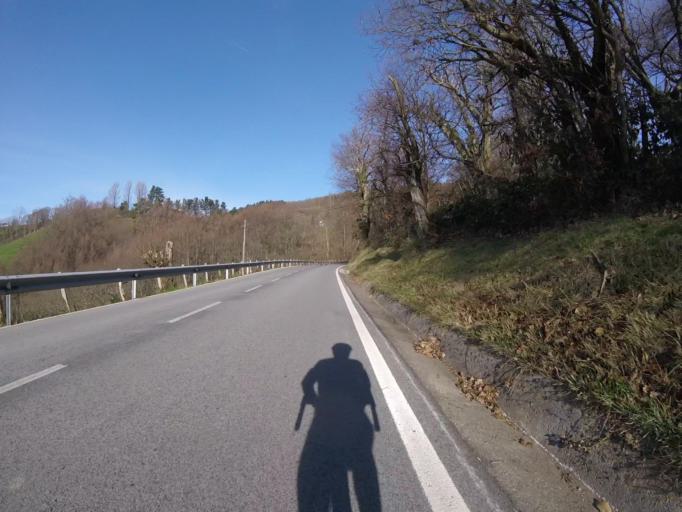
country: ES
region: Navarre
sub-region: Provincia de Navarra
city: Leitza
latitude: 43.0869
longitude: -1.9043
